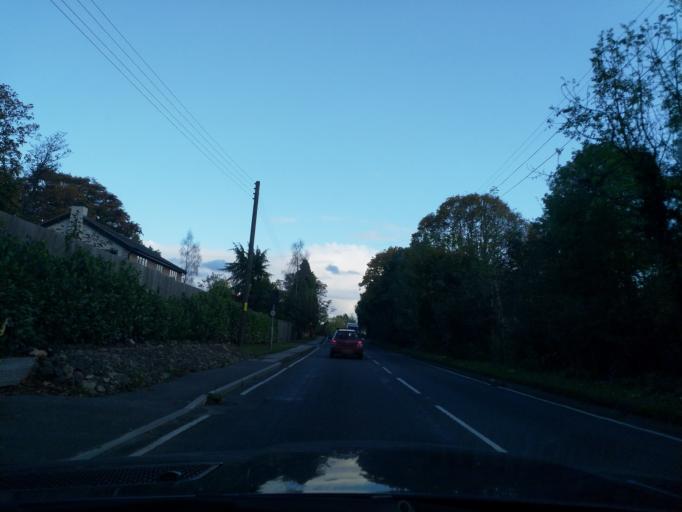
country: GB
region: England
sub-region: Solihull
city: Knowle
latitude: 52.3430
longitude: -1.7596
